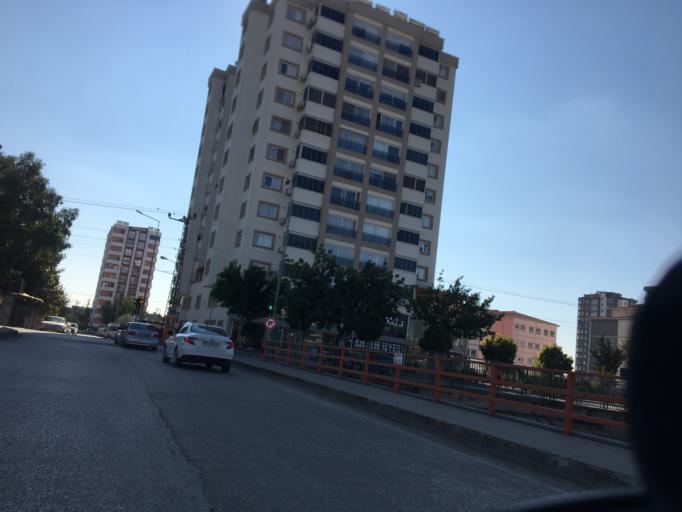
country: TR
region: Adana
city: Seyhan
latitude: 37.0110
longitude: 35.2974
